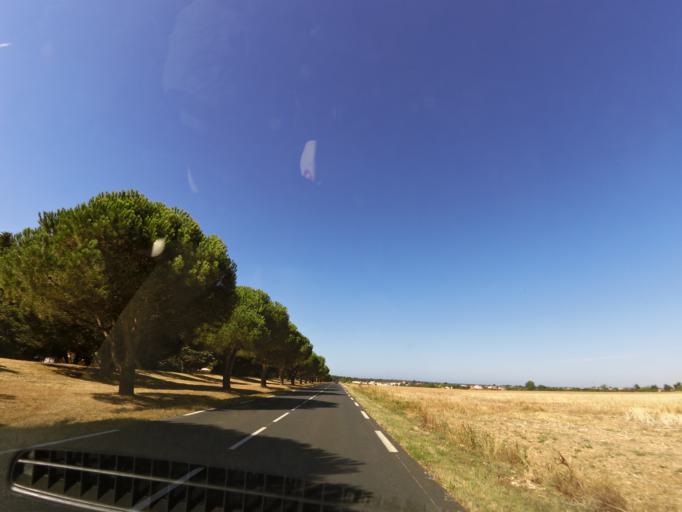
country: FR
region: Pays de la Loire
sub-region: Departement de la Vendee
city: Longeville-sur-Mer
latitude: 46.4184
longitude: -1.5316
